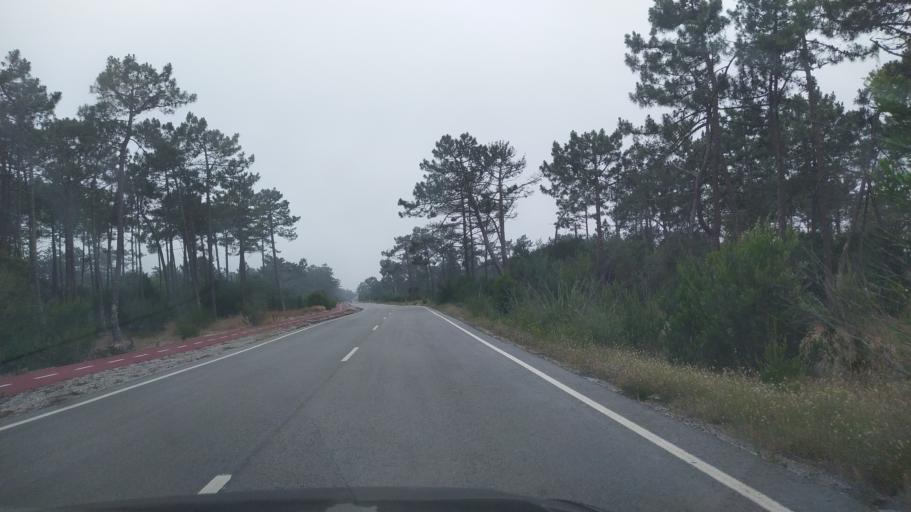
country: PT
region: Aveiro
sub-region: Ilhavo
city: Gafanha da Encarnacao
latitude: 40.5695
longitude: -8.7381
